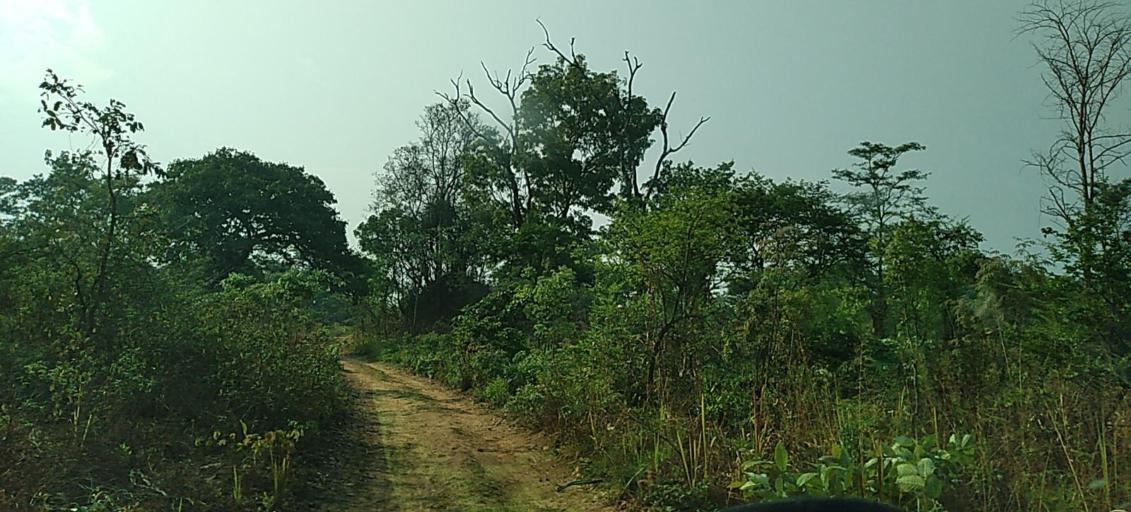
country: ZM
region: North-Western
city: Solwezi
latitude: -12.3972
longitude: 26.5825
